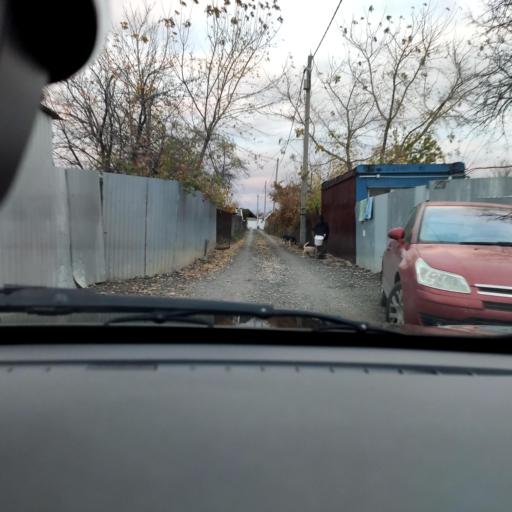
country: RU
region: Samara
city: Tol'yatti
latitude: 53.5403
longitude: 49.4292
